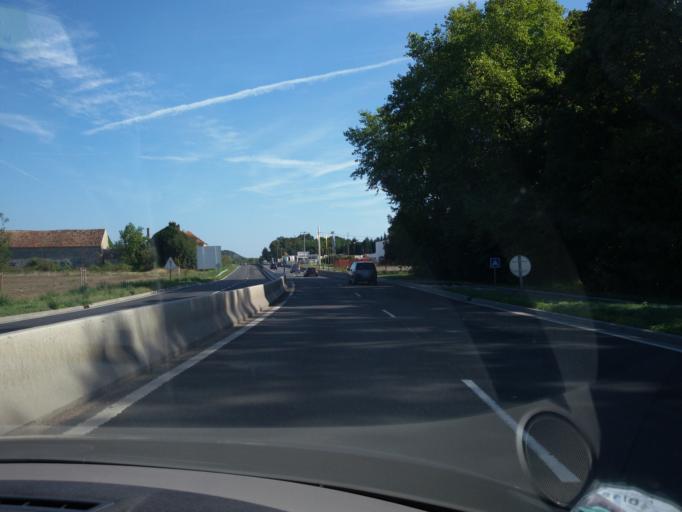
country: FR
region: Ile-de-France
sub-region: Departement de l'Essonne
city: Morigny-Champigny
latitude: 48.4588
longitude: 2.1775
